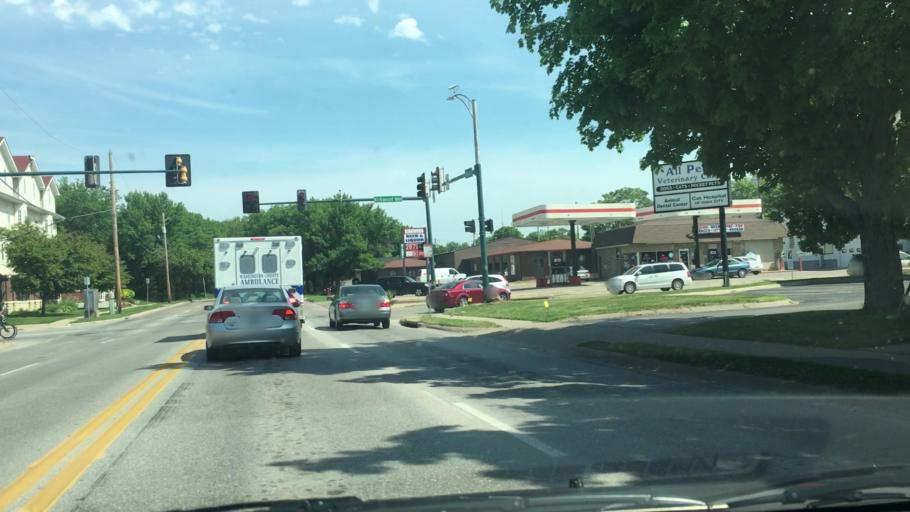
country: US
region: Iowa
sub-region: Johnson County
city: Iowa City
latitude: 41.6491
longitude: -91.5320
